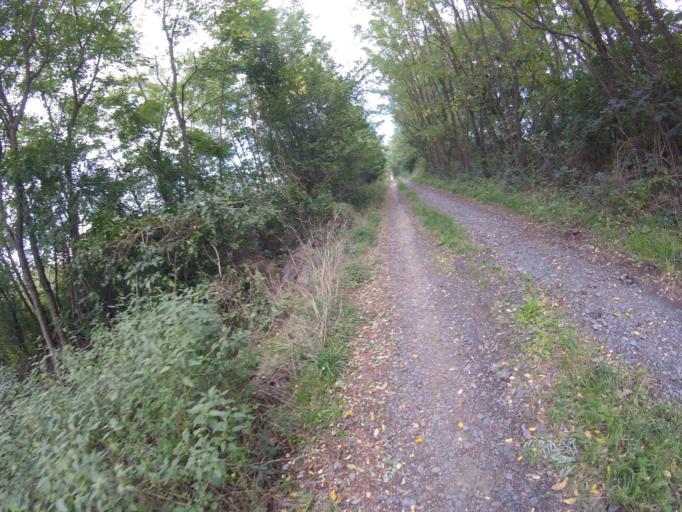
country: HU
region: Vas
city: Csepreg
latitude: 47.3773
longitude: 16.6762
